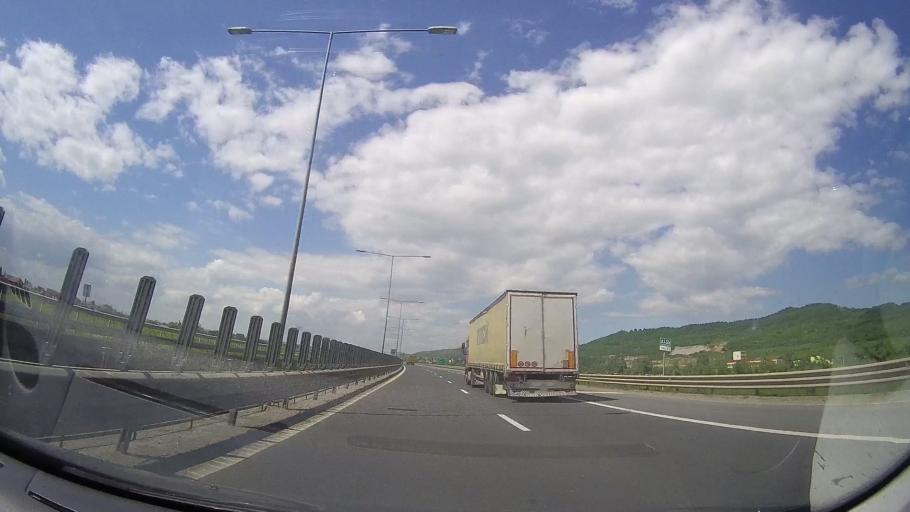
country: RO
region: Sibiu
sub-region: Comuna Selimbar
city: Selimbar
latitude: 45.7937
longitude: 24.1967
